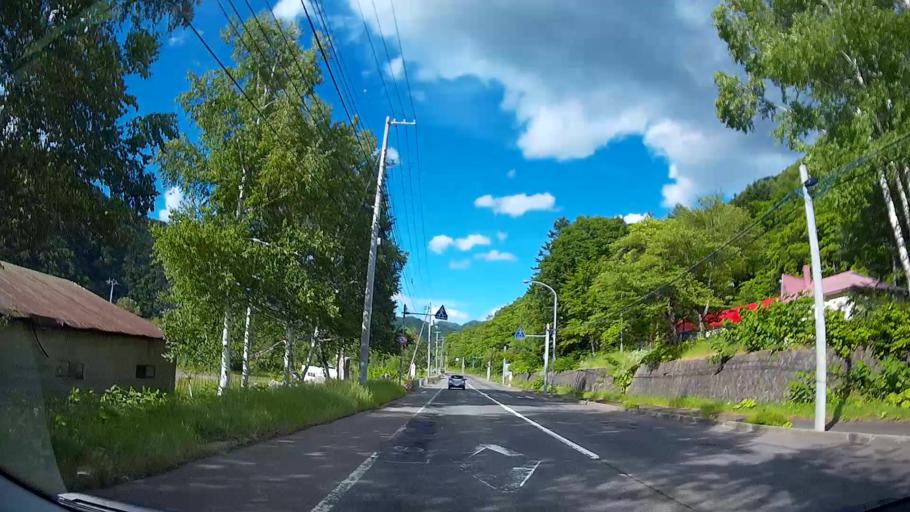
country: JP
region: Hokkaido
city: Sapporo
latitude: 42.9573
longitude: 141.1545
